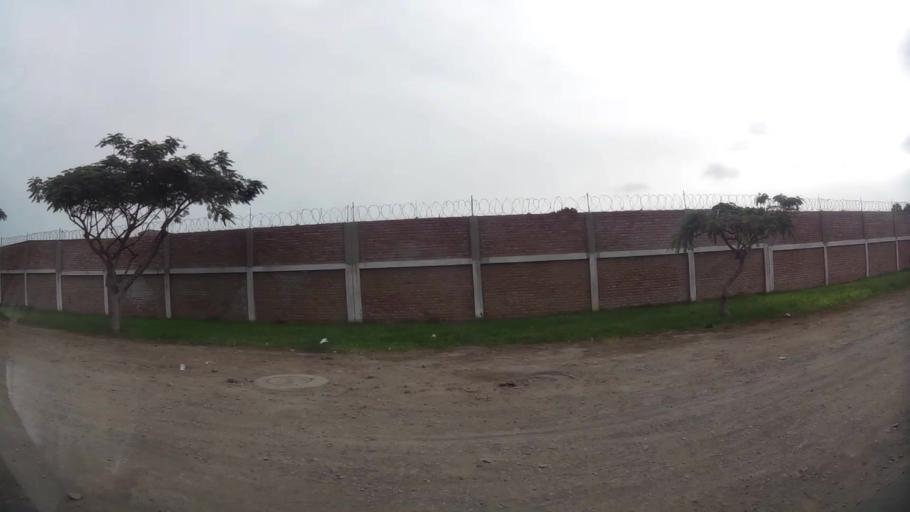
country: PE
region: Callao
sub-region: Callao
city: Callao
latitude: -12.0113
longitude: -77.1115
